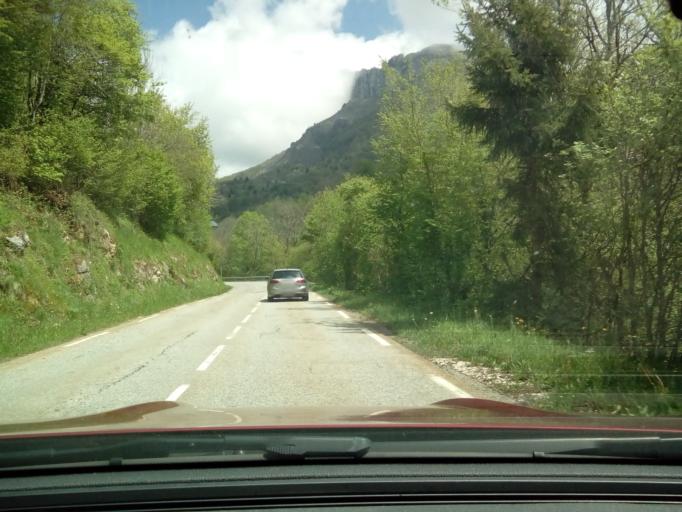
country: FR
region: Rhone-Alpes
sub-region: Departement de la Savoie
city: Barby
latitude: 45.6141
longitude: 6.0148
